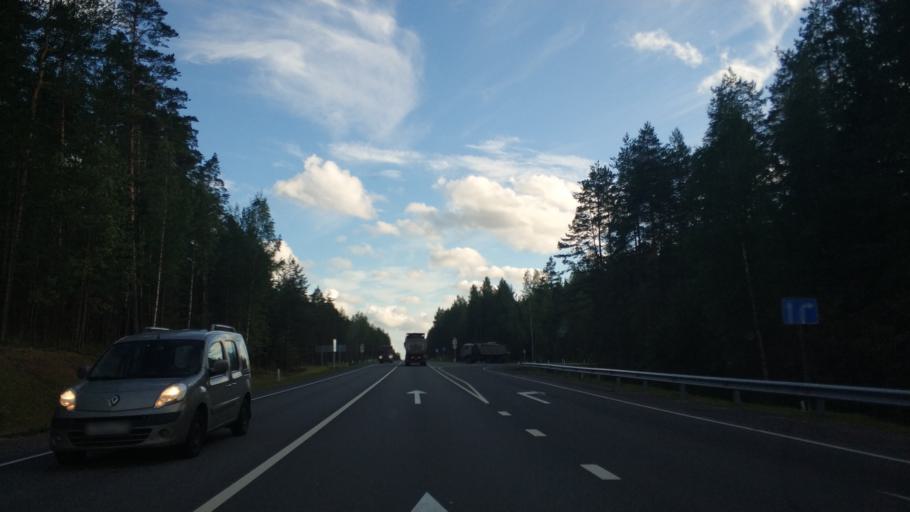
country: RU
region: Leningrad
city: Priozersk
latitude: 60.8729
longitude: 30.1623
